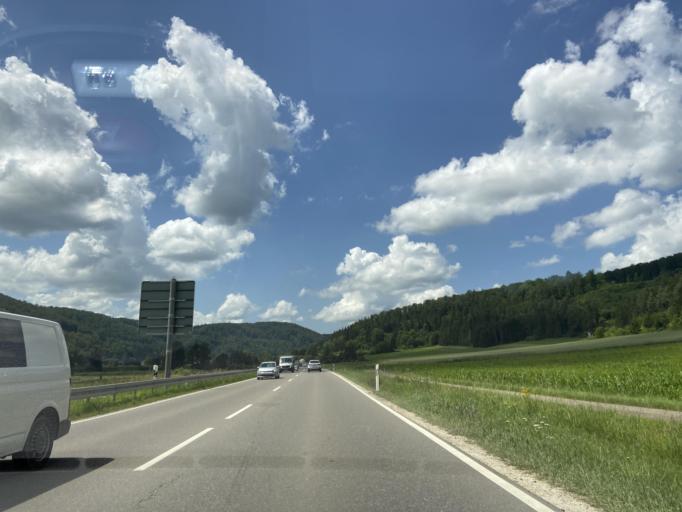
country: DE
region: Baden-Wuerttemberg
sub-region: Tuebingen Region
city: Strassberg
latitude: 48.1931
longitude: 9.0814
